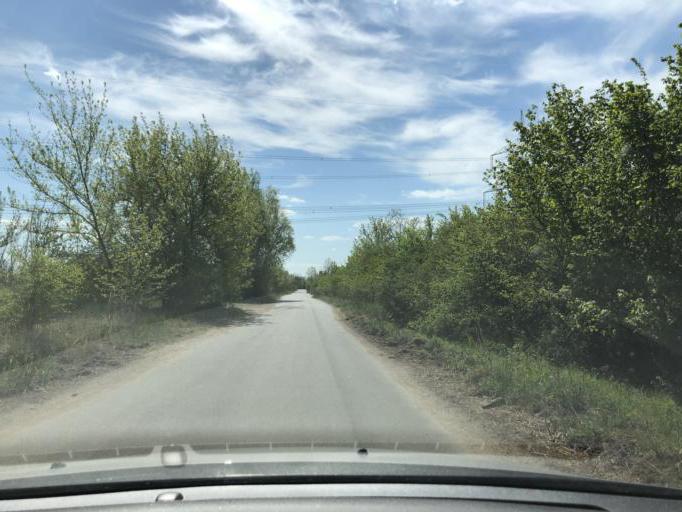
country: DE
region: Saxony-Anhalt
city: Dieskau
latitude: 51.4483
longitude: 11.9990
